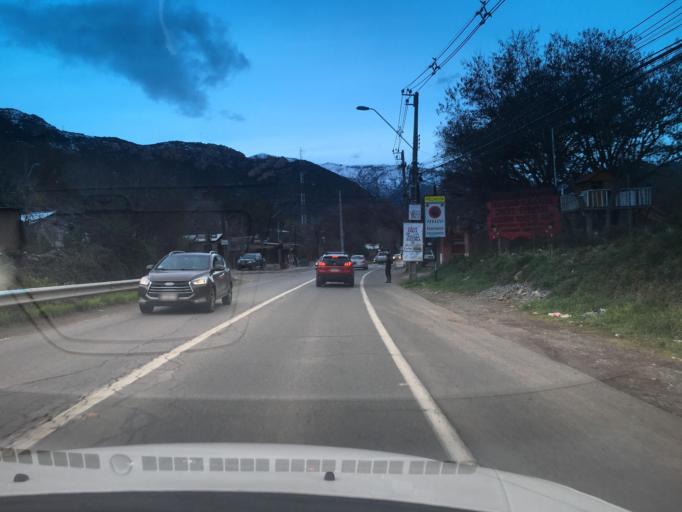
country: CL
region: Santiago Metropolitan
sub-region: Provincia de Cordillera
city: Puente Alto
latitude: -33.5817
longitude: -70.4020
